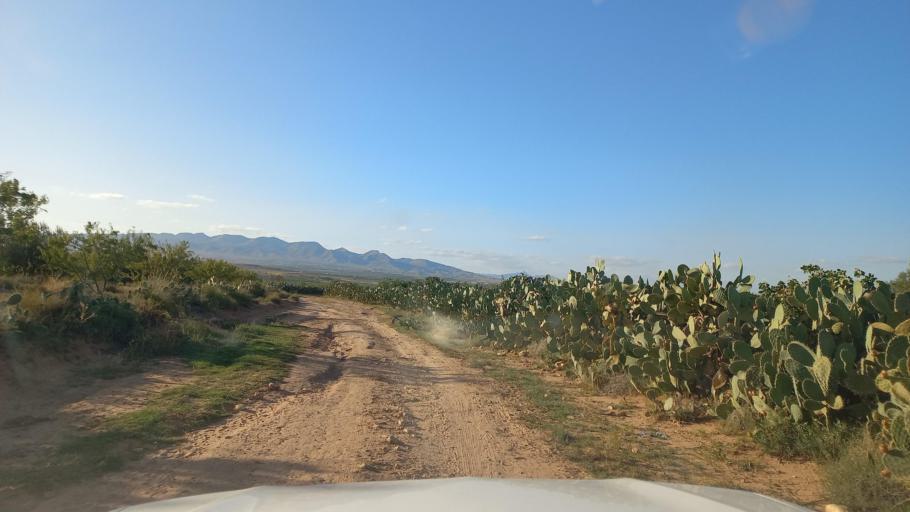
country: TN
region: Al Qasrayn
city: Sbiba
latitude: 35.3856
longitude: 9.1558
